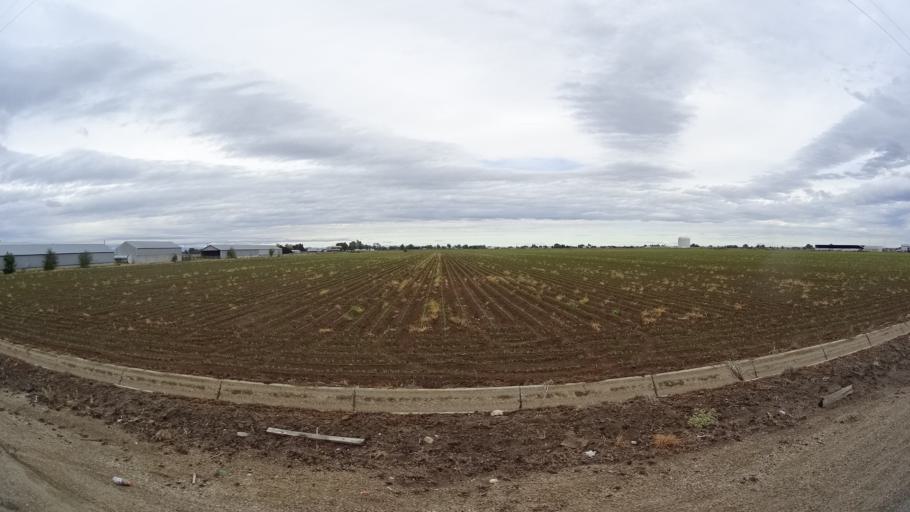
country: US
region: Idaho
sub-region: Ada County
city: Star
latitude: 43.6365
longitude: -116.4936
